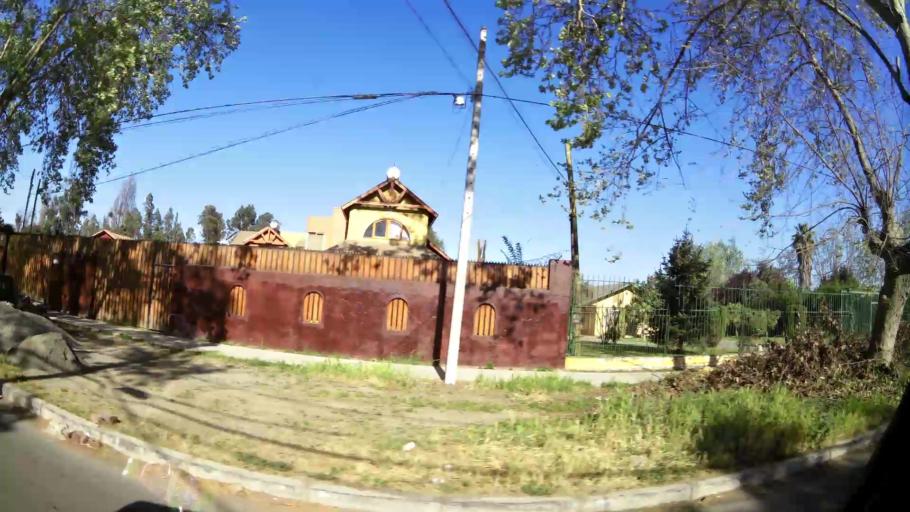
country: CL
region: Santiago Metropolitan
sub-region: Provincia de Talagante
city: Penaflor
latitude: -33.6040
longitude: -70.8700
